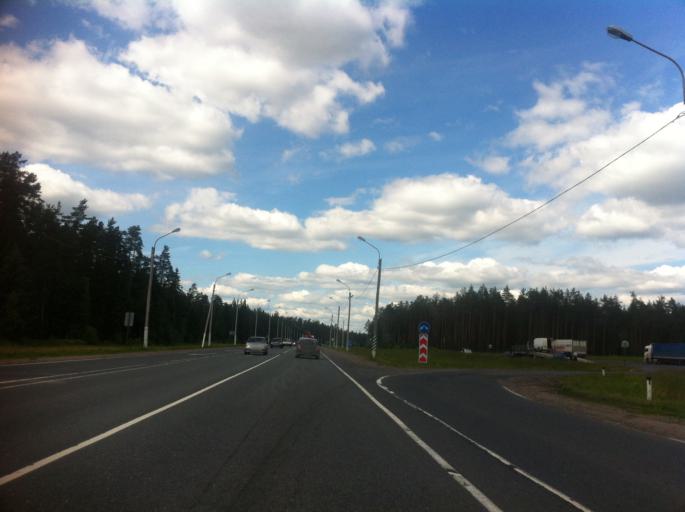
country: RU
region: Leningrad
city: Luga
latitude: 58.7140
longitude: 29.8790
